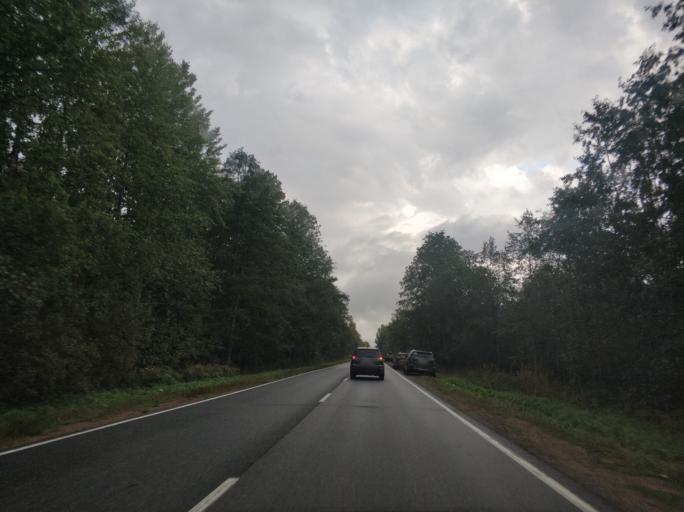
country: RU
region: Leningrad
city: Borisova Griva
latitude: 60.1369
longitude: 30.9570
